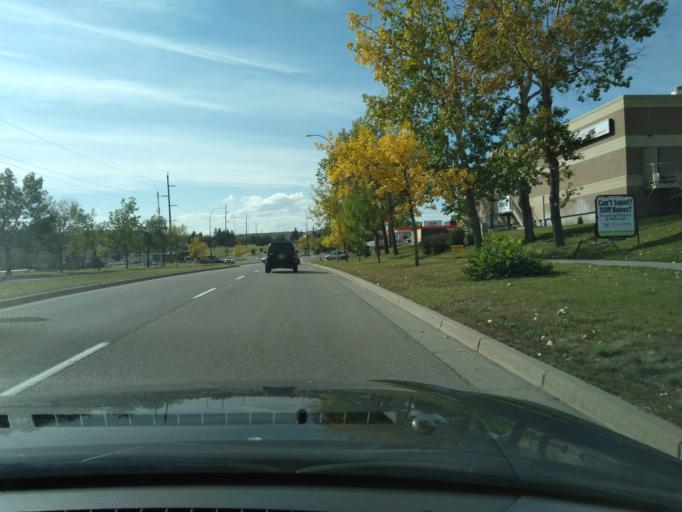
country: CA
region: Alberta
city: Calgary
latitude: 51.1253
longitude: -114.0688
